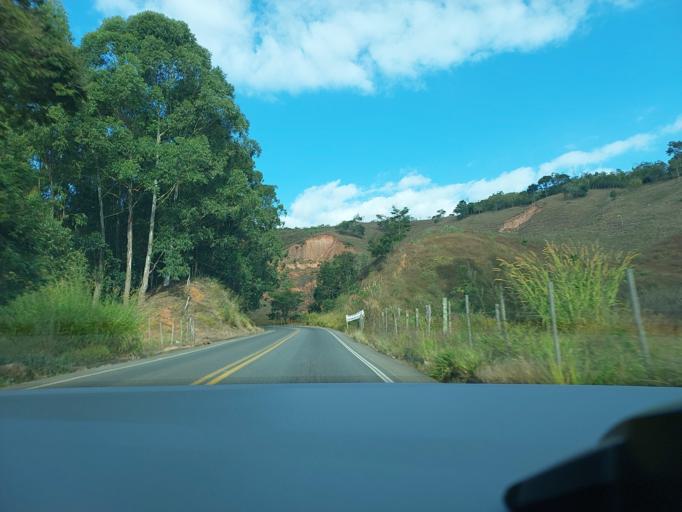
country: BR
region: Minas Gerais
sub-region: Vicosa
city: Vicosa
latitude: -20.8383
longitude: -42.7196
